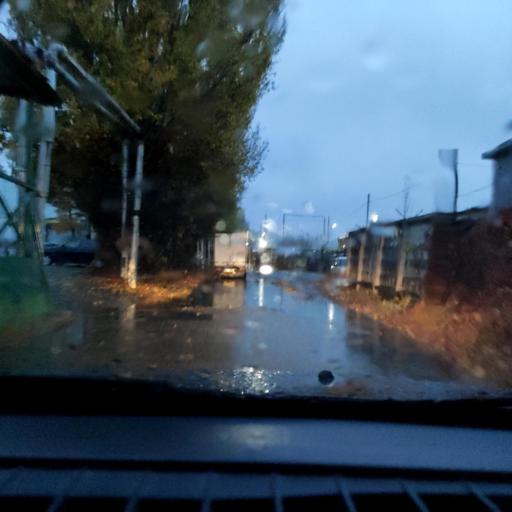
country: RU
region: Samara
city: Tol'yatti
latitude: 53.5454
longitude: 49.2995
